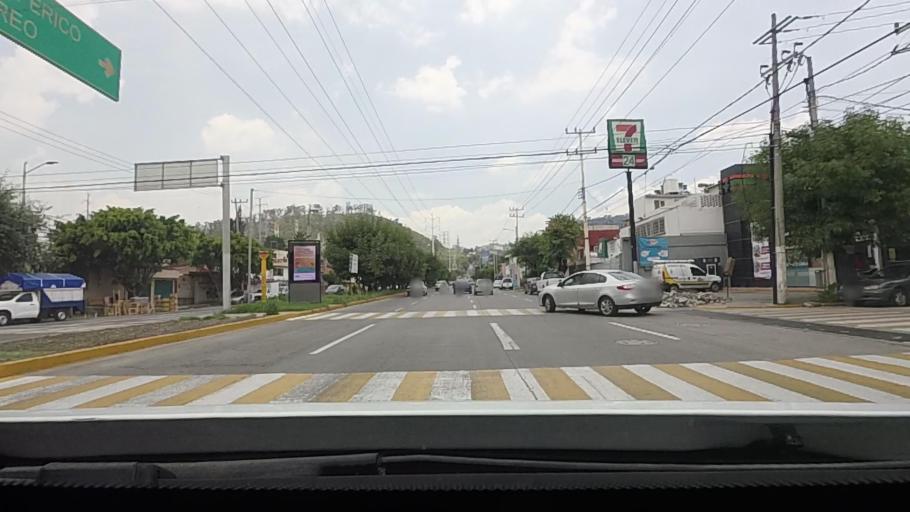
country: MX
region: Mexico
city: Naucalpan de Juarez
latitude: 19.4895
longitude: -99.2562
